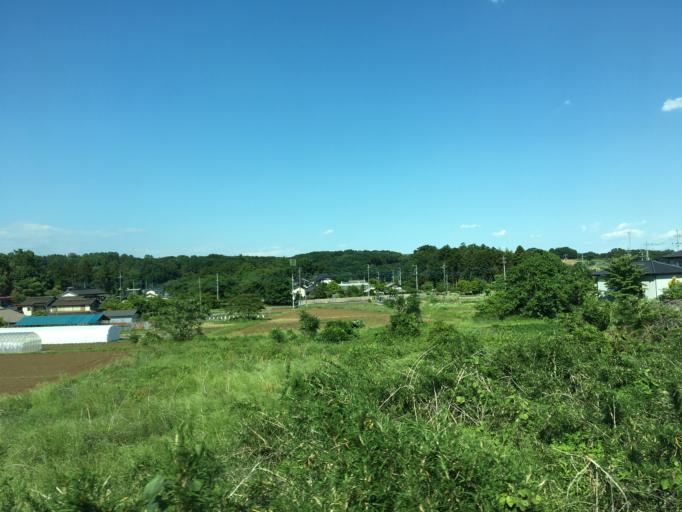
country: JP
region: Saitama
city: Morohongo
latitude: 35.9784
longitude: 139.3352
